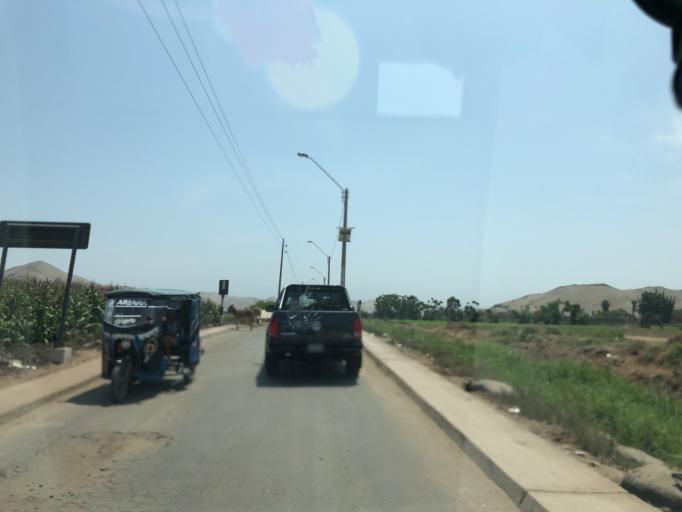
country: PE
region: Lima
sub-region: Provincia de Canete
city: San Vicente de Canete
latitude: -13.0236
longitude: -76.4744
